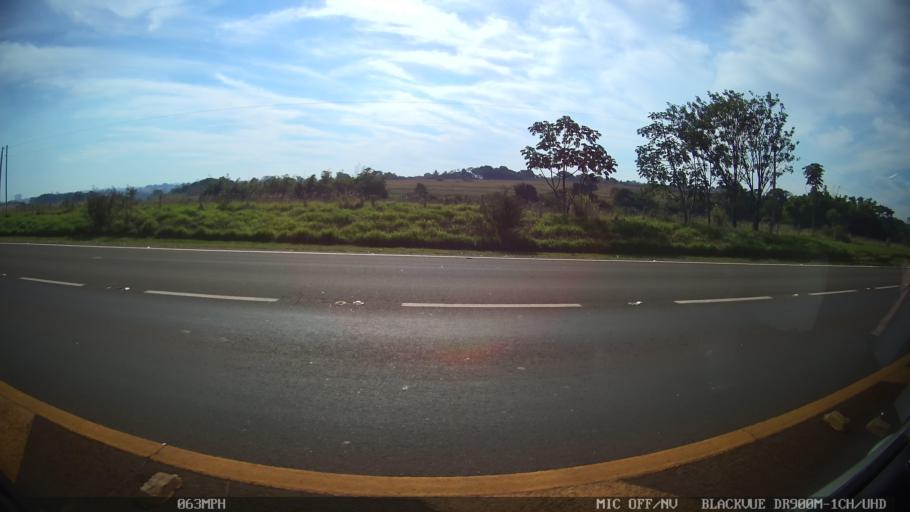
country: BR
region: Sao Paulo
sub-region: Araraquara
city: Araraquara
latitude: -21.7907
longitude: -48.1278
